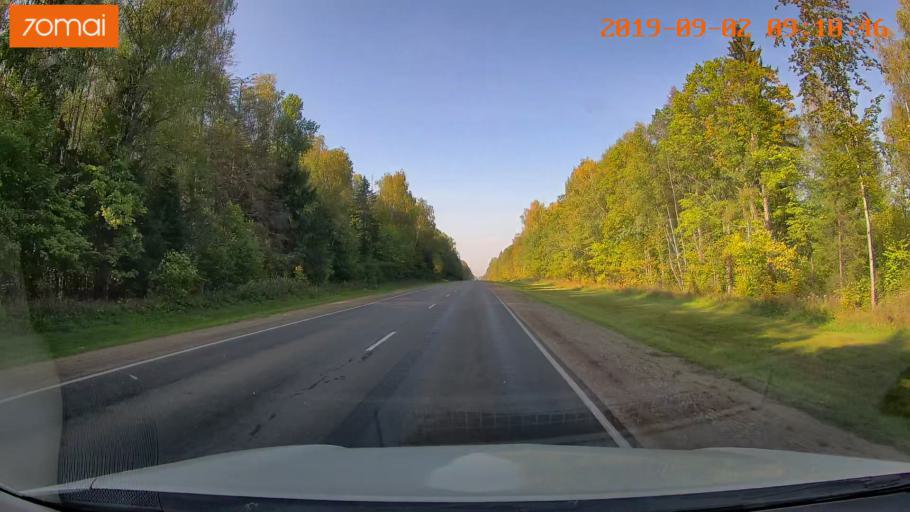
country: RU
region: Kaluga
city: Myatlevo
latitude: 54.8732
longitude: 35.5922
